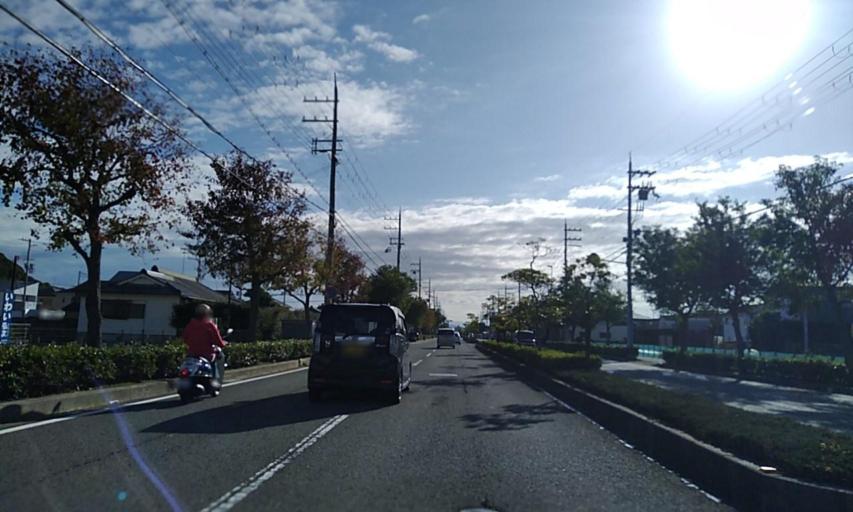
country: JP
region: Wakayama
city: Minato
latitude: 34.2614
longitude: 135.1031
